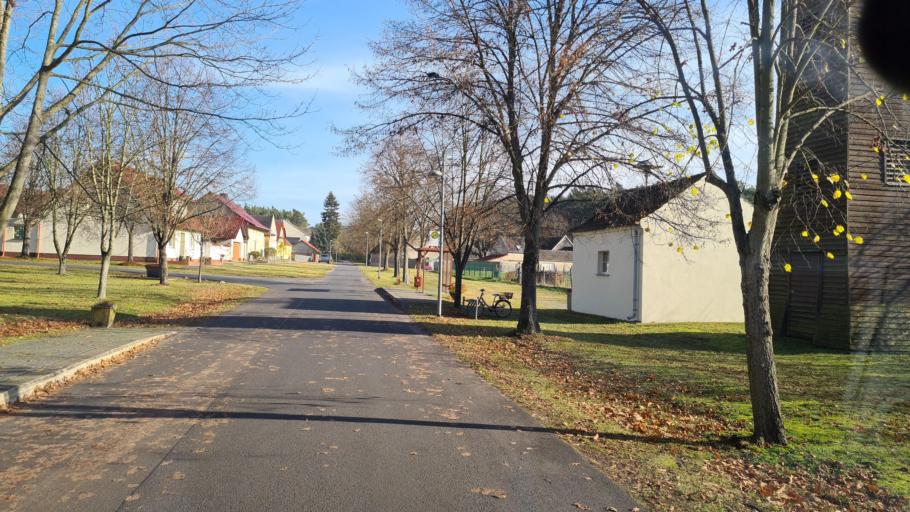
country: DE
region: Brandenburg
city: Golzow
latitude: 52.2802
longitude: 12.6401
